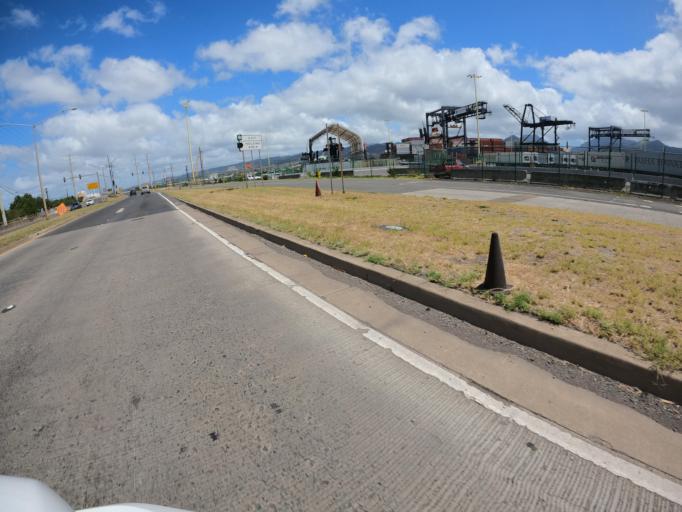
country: US
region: Hawaii
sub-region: Honolulu County
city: Honolulu
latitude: 21.3121
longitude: -157.8868
